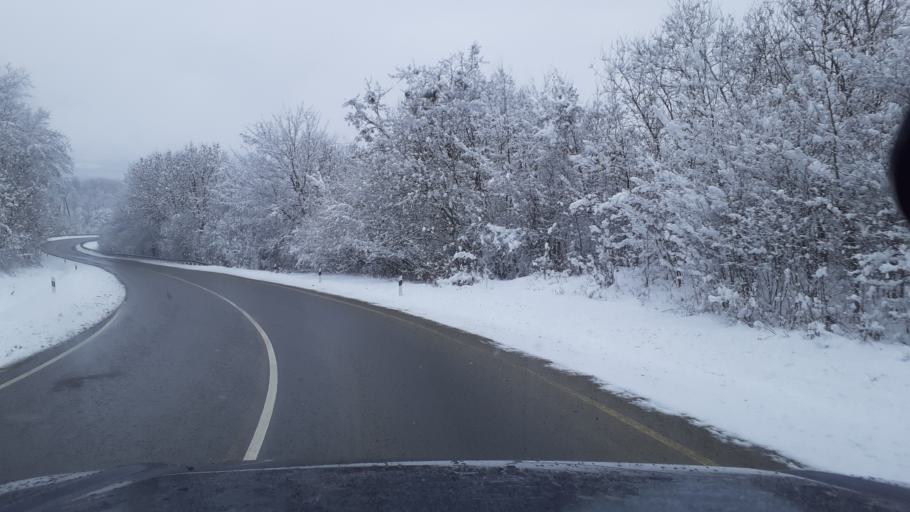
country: RU
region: Adygeya
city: Kamennomostskiy
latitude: 44.2134
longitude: 40.1861
